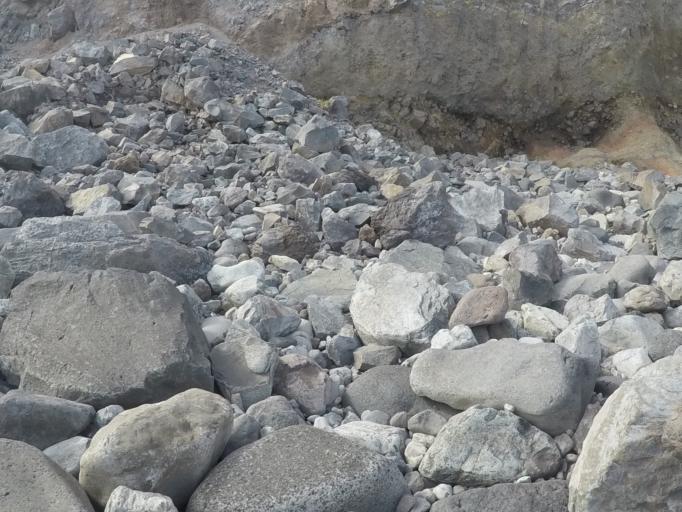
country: PT
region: Madeira
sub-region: Sao Vicente
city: Sao Vicente
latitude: 32.8090
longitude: -16.9685
